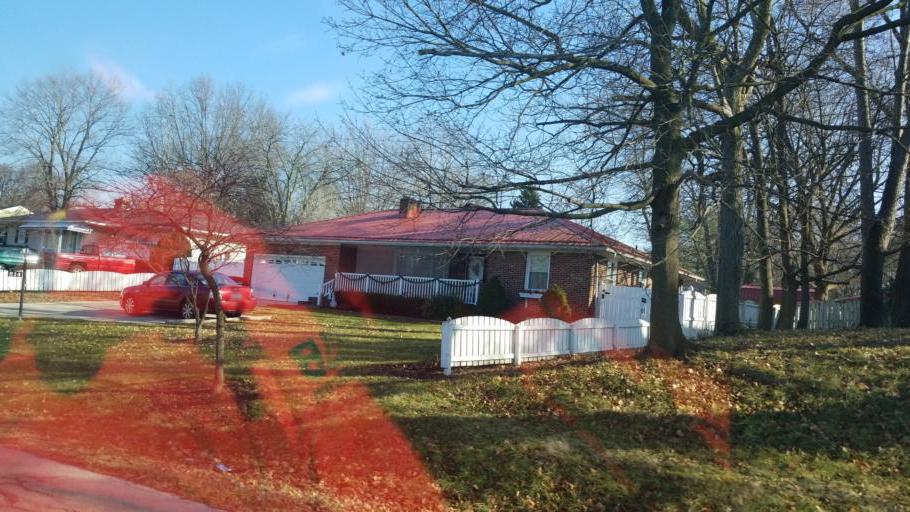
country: US
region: Ohio
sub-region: Seneca County
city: Tiffin
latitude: 41.1212
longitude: -83.1722
